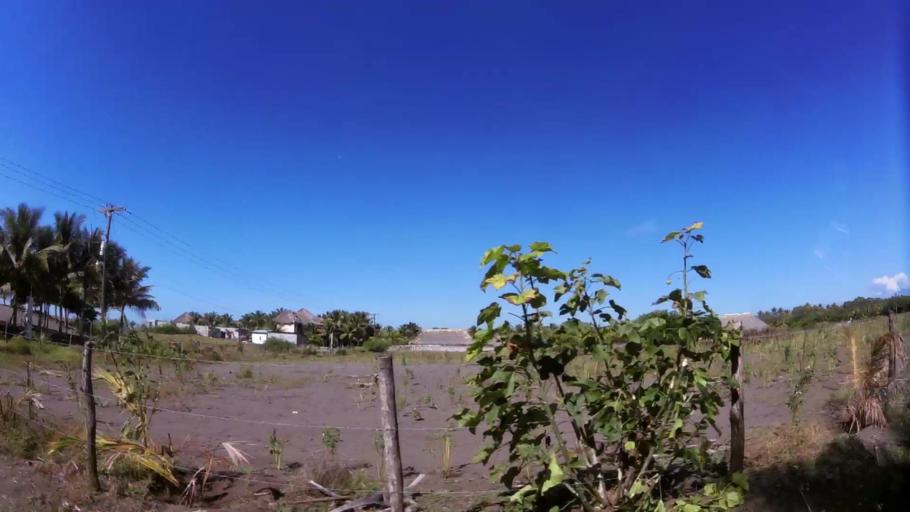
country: GT
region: Santa Rosa
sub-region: Municipio de Taxisco
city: Taxisco
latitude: 13.8821
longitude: -90.4567
